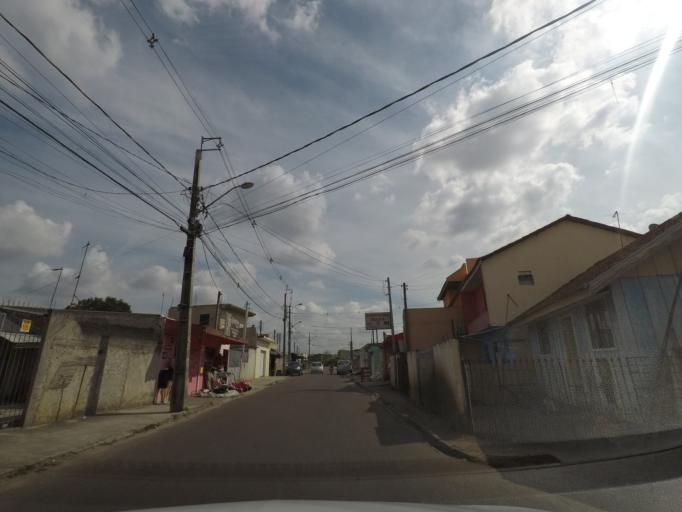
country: BR
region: Parana
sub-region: Sao Jose Dos Pinhais
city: Sao Jose dos Pinhais
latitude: -25.4903
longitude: -49.2010
